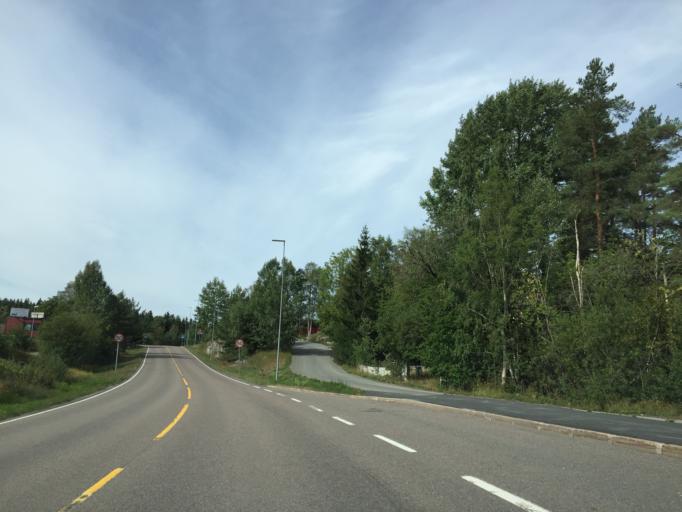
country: NO
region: Akershus
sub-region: Vestby
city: Vestby
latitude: 59.5188
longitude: 10.7093
